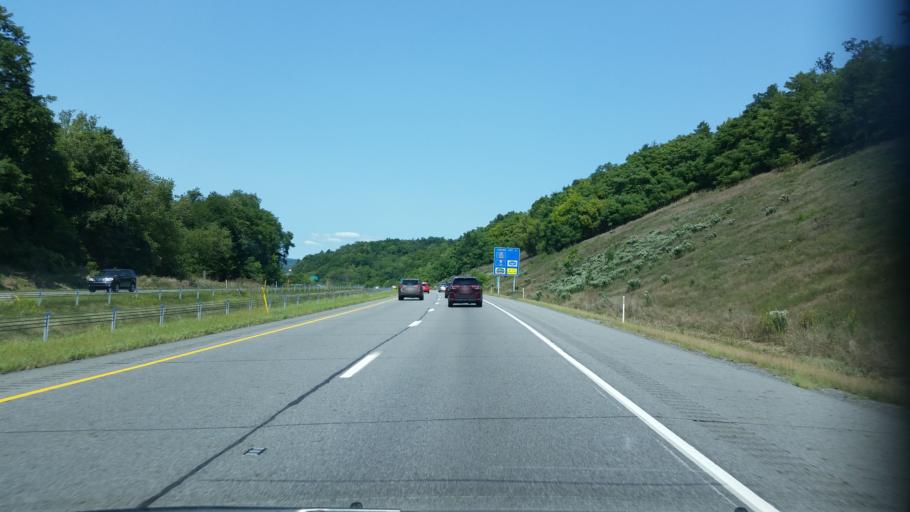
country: US
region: Pennsylvania
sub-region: Blair County
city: Duncansville
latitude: 40.4488
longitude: -78.4218
